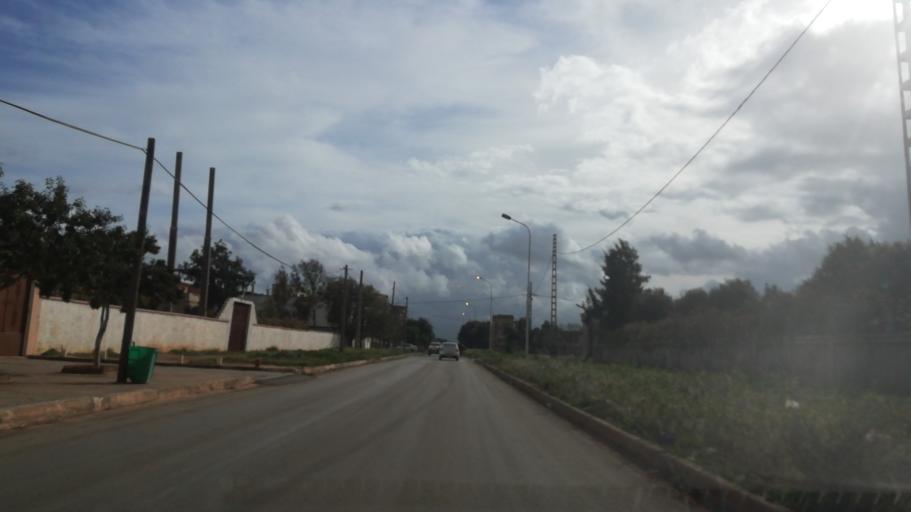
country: DZ
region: Oran
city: Es Senia
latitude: 35.6605
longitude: -0.6382
